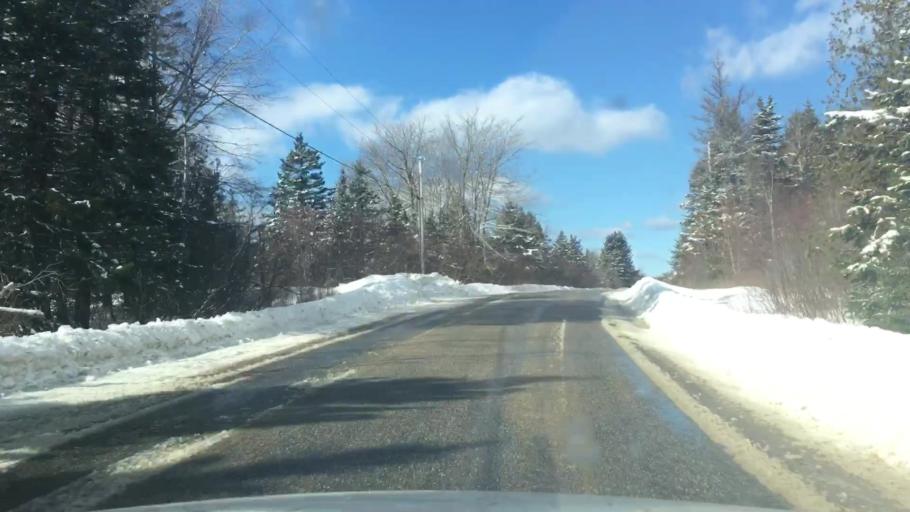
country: US
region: Maine
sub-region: Washington County
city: Machias
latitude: 44.6805
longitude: -67.4553
